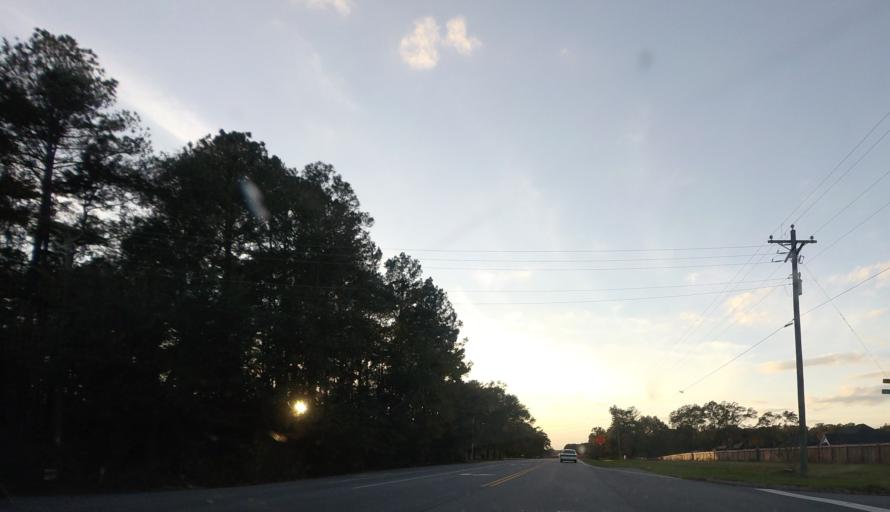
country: US
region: Georgia
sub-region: Houston County
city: Robins Air Force Base
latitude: 32.5436
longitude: -83.5642
